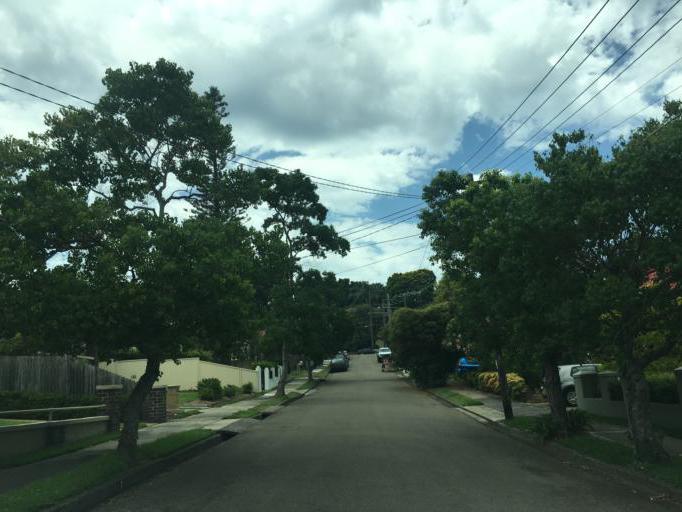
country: AU
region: New South Wales
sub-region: Hunters Hill
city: Gladesville
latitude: -33.8343
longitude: 151.1238
